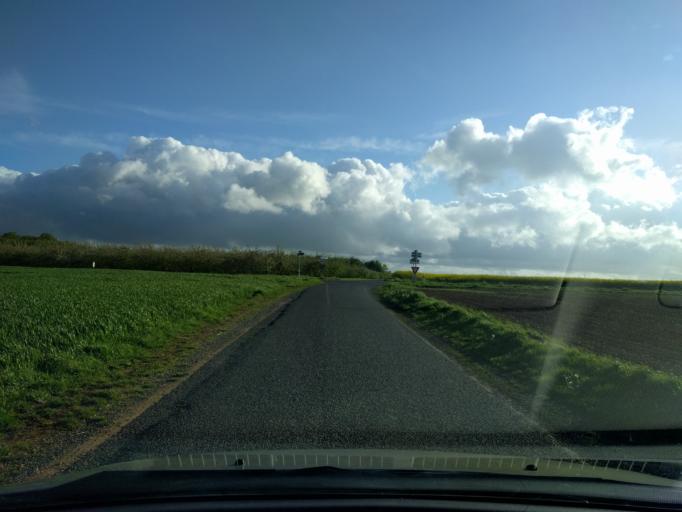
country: FR
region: Haute-Normandie
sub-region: Departement de l'Eure
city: Damville
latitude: 48.8846
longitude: 1.0540
